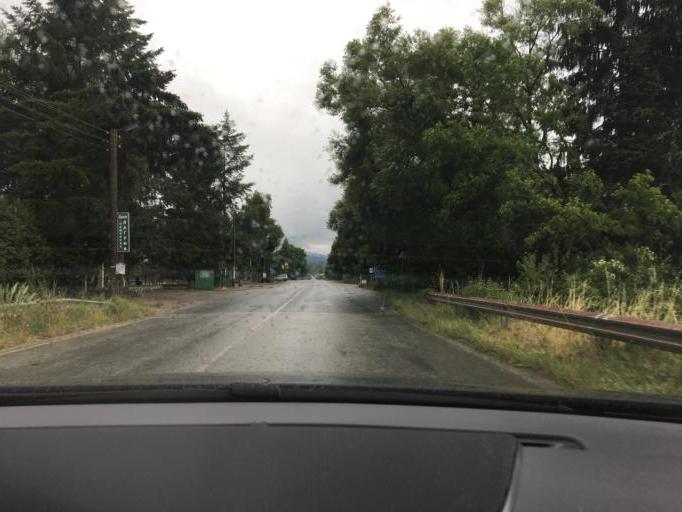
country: BG
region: Kyustendil
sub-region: Obshtina Kyustendil
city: Kyustendil
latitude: 42.2564
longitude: 22.5503
